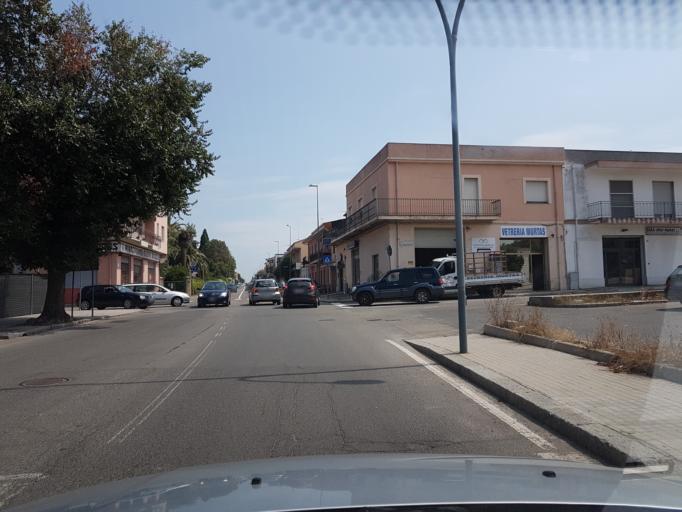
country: IT
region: Sardinia
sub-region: Provincia di Oristano
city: Oristano
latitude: 39.9076
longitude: 8.6002
